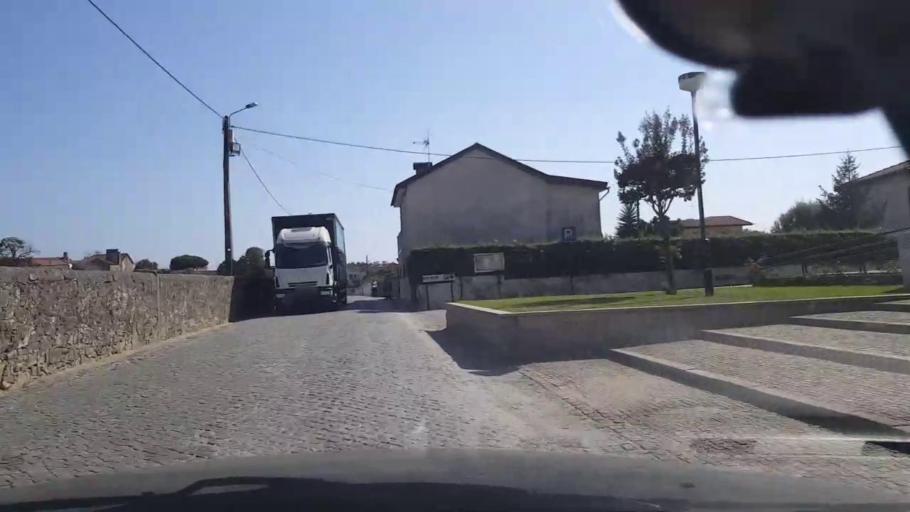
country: PT
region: Porto
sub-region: Povoa de Varzim
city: Pedroso
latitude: 41.4029
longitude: -8.6868
